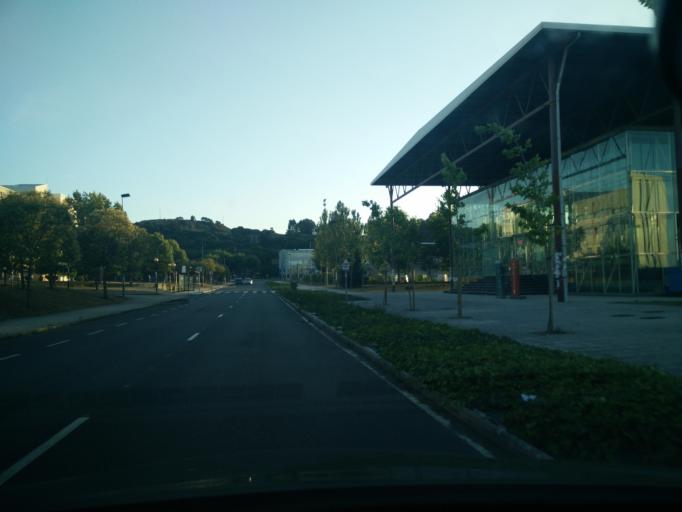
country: ES
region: Galicia
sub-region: Provincia da Coruna
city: A Coruna
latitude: 43.3341
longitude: -8.4101
